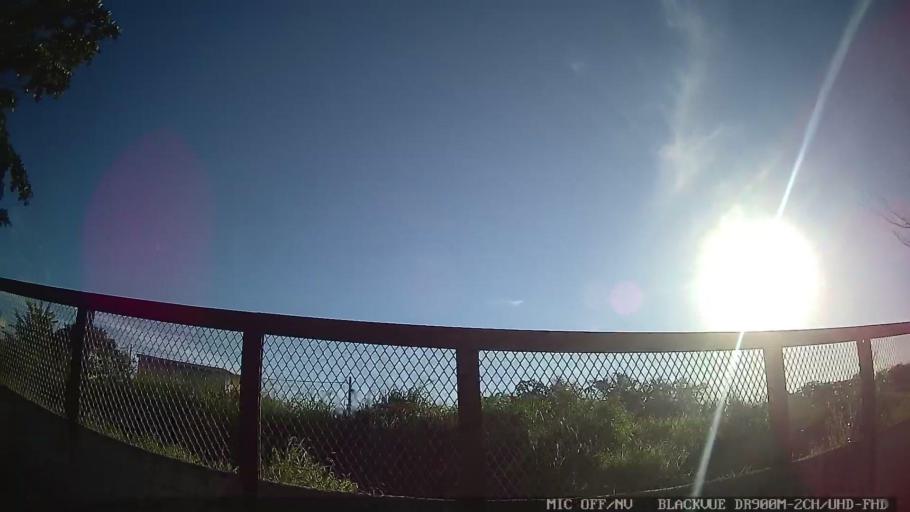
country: BR
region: Sao Paulo
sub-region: Santos
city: Santos
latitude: -23.9452
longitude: -46.3061
